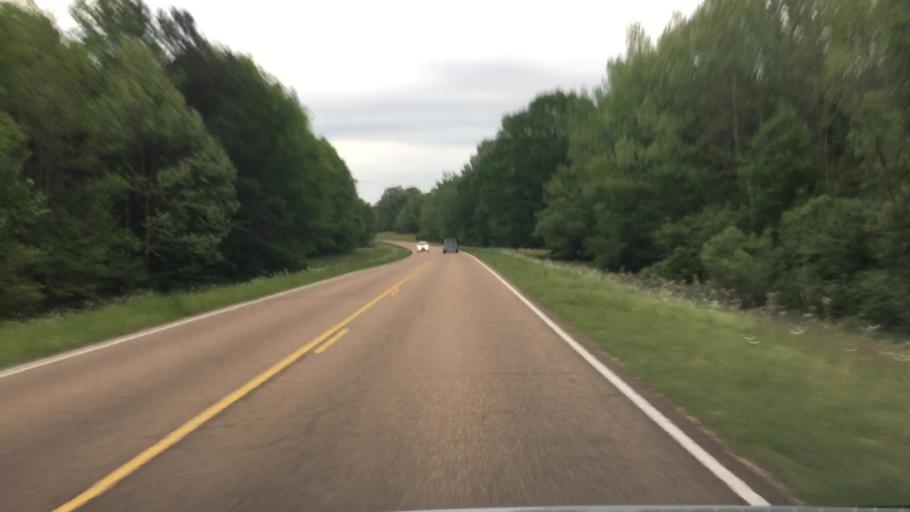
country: US
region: Mississippi
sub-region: Hinds County
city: Clinton
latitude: 32.3897
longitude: -90.2538
